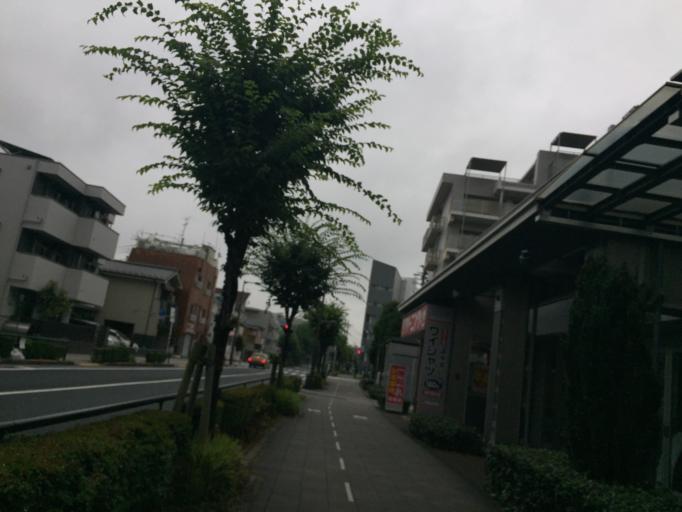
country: JP
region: Tokyo
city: Tokyo
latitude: 35.6386
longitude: 139.6736
